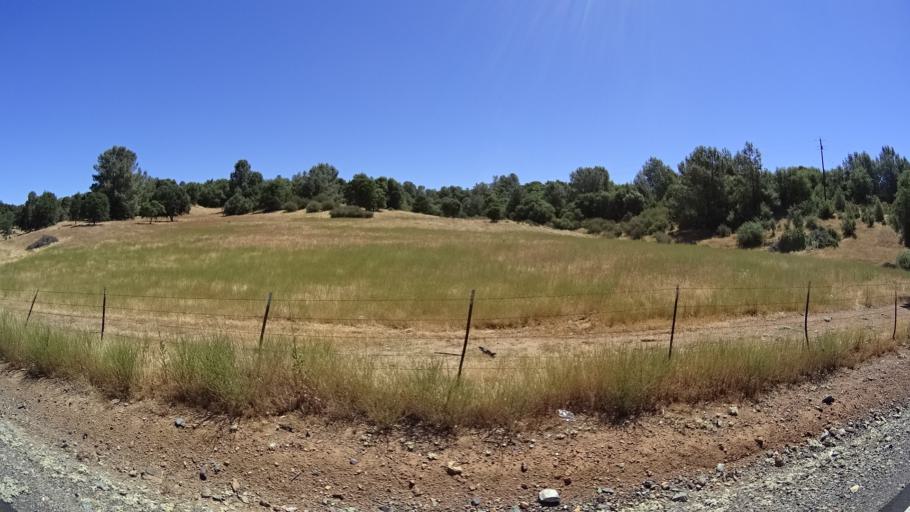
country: US
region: California
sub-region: Calaveras County
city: Copperopolis
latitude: 38.0318
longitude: -120.6481
